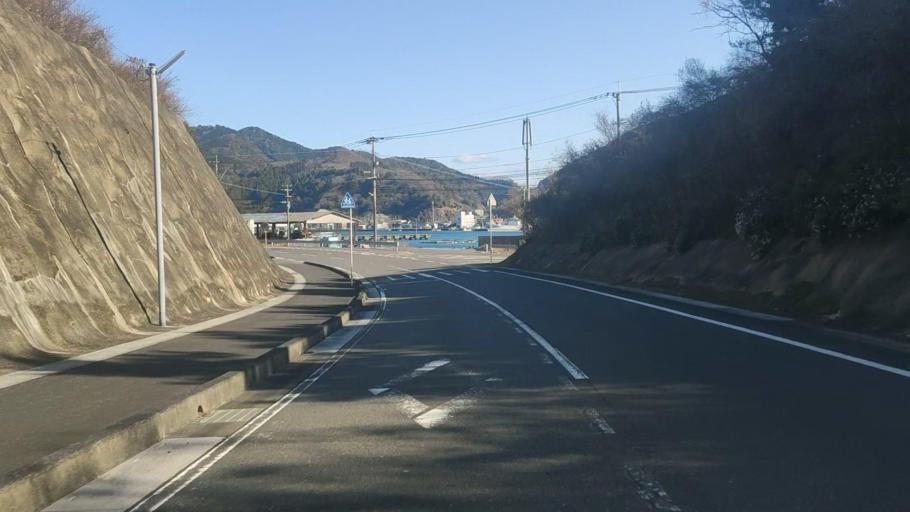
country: JP
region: Oita
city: Saiki
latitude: 32.7968
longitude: 131.9167
